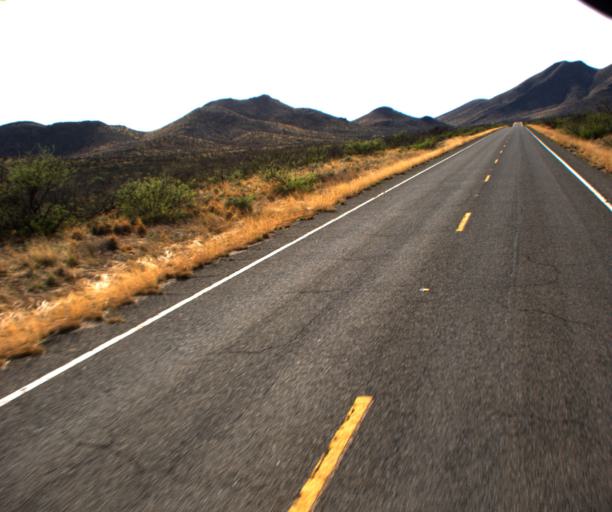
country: US
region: Arizona
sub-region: Cochise County
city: Willcox
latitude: 32.1786
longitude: -109.6297
